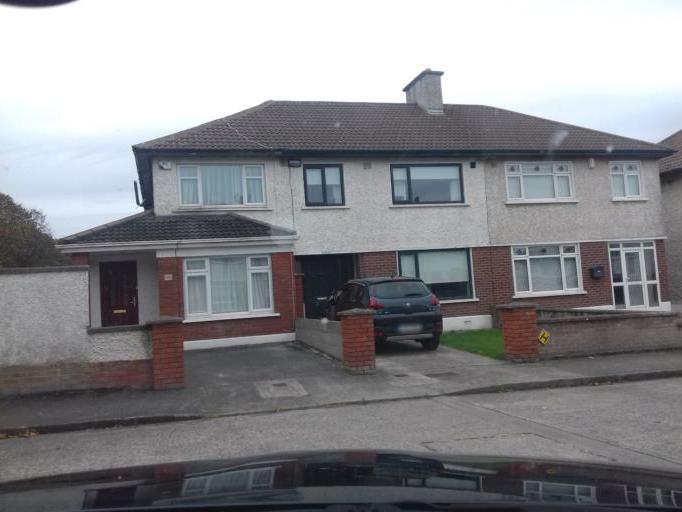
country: IE
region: Leinster
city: Artane
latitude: 53.3847
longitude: -6.2230
